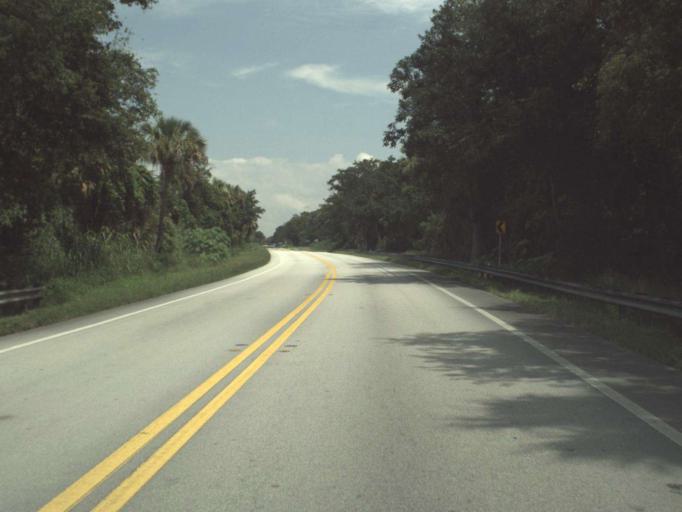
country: US
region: Florida
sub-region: Martin County
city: Indiantown
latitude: 26.9666
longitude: -80.6106
